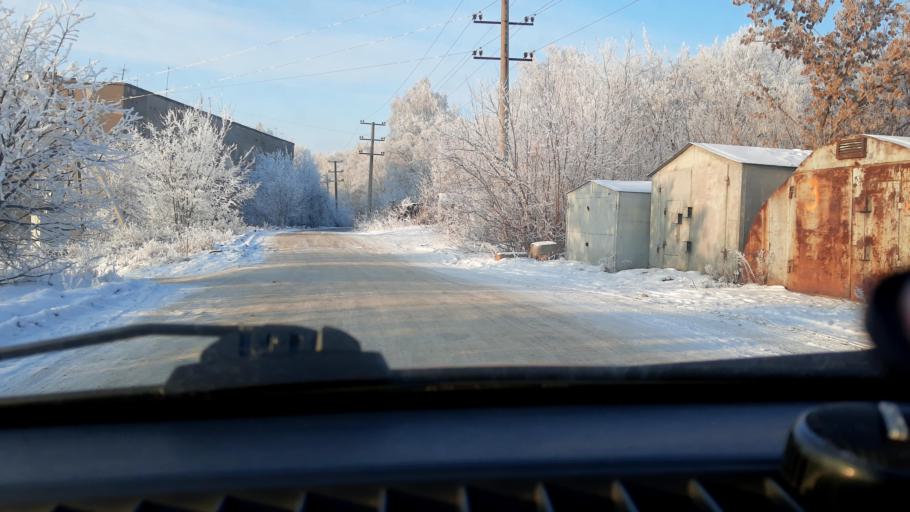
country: RU
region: Bashkortostan
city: Iglino
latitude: 54.7712
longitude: 56.2424
